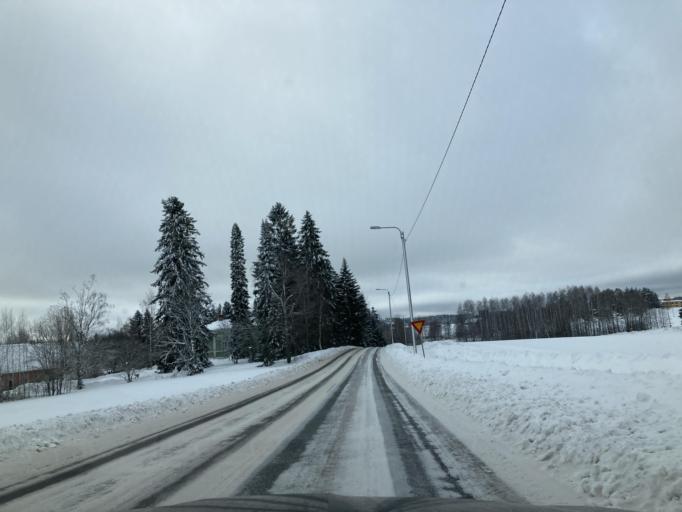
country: FI
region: Central Finland
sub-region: Jaemsae
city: Jaemsae
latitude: 61.8598
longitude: 25.2277
